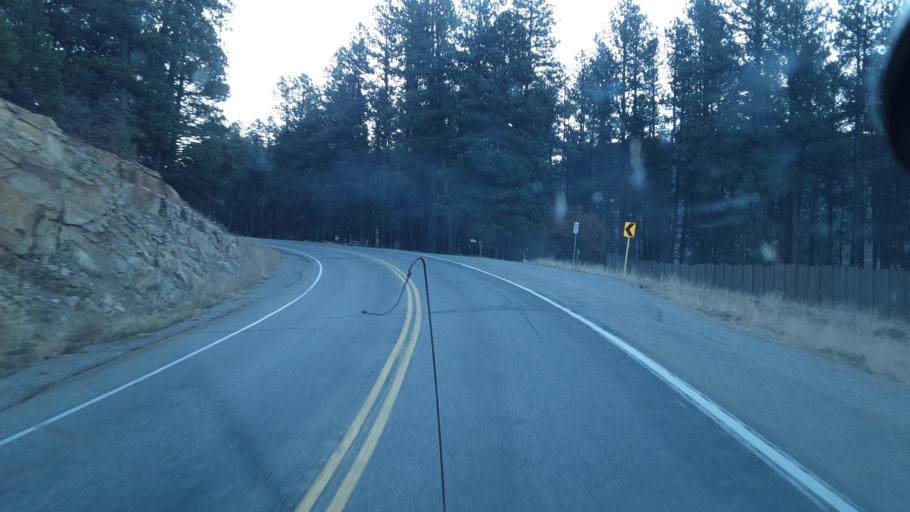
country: US
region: Colorado
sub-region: La Plata County
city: Durango
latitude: 37.3313
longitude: -107.7369
